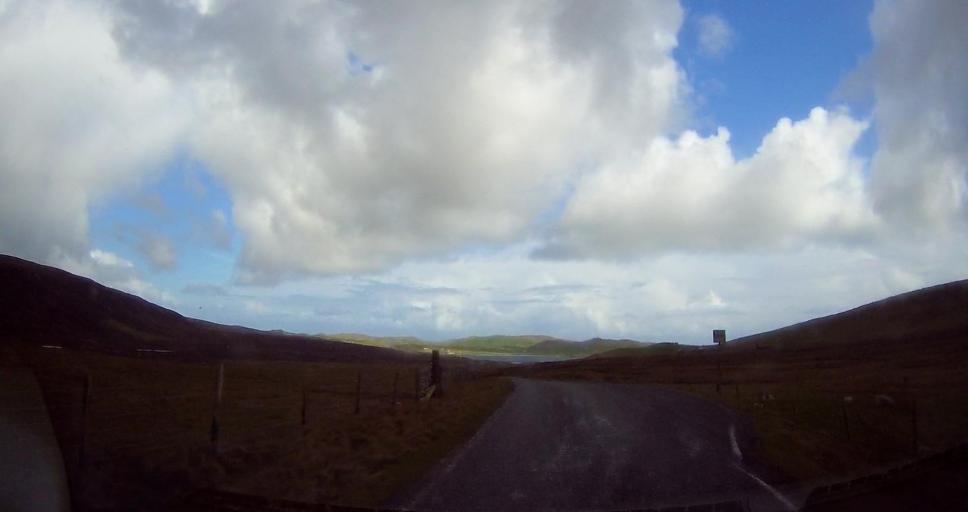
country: GB
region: Scotland
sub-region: Shetland Islands
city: Lerwick
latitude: 60.5622
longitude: -1.3351
